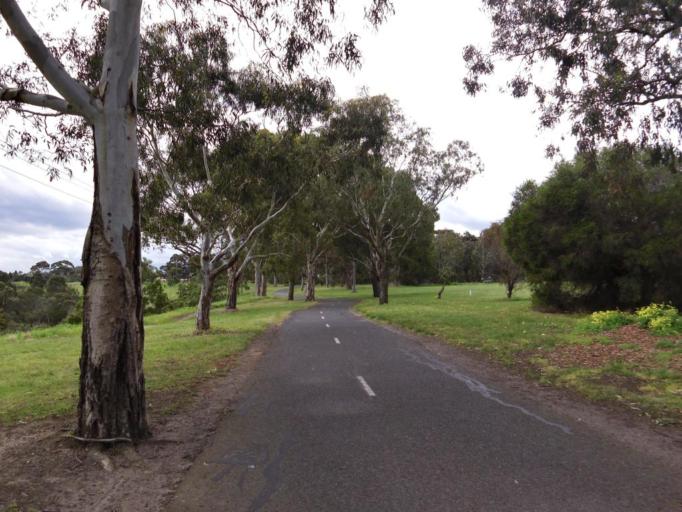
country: AU
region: Victoria
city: Abbotsford
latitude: -37.7904
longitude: 145.0080
